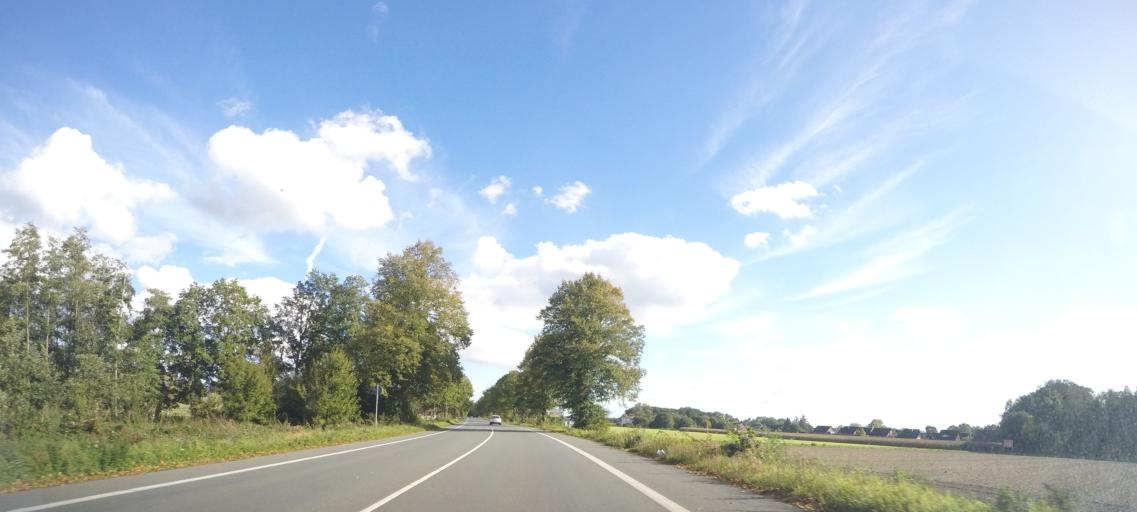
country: DE
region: North Rhine-Westphalia
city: Ahlen
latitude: 51.6979
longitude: 7.9336
